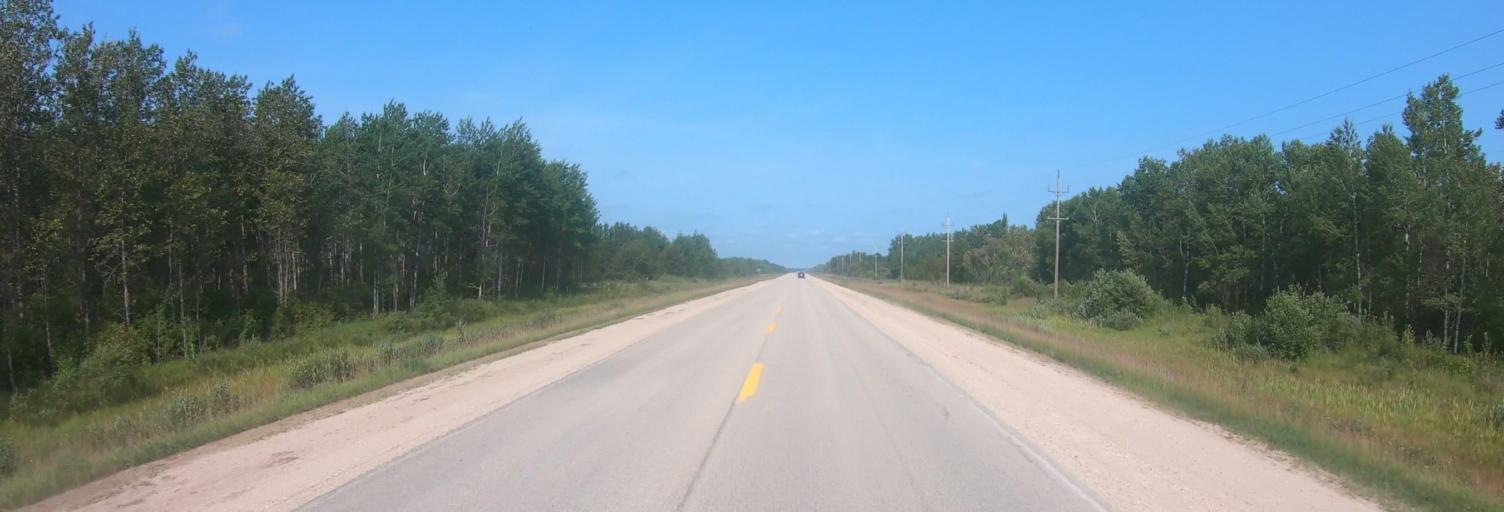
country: US
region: Minnesota
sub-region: Roseau County
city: Roseau
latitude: 49.1420
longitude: -96.1074
